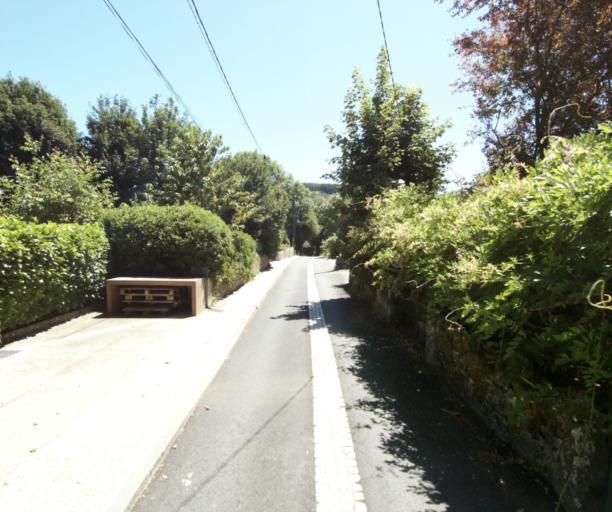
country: FR
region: Midi-Pyrenees
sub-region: Departement du Tarn
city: Dourgne
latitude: 43.4292
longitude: 2.1688
